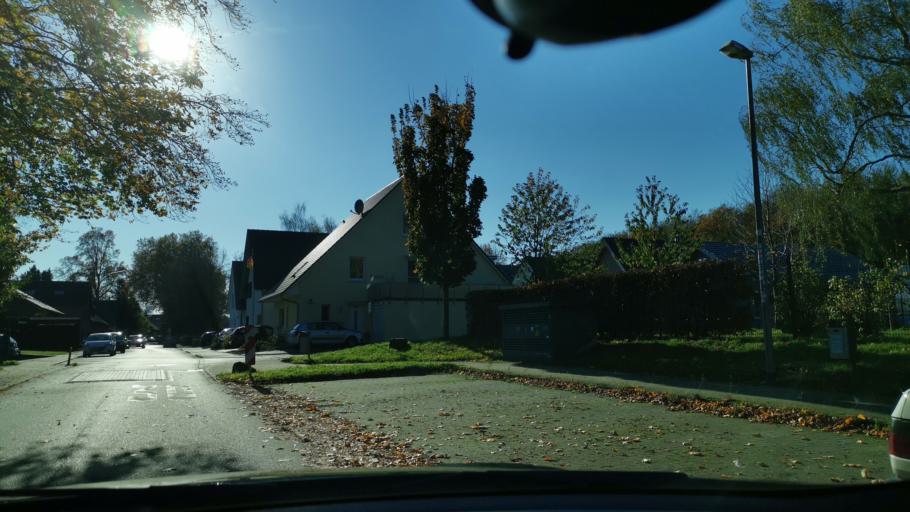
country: DE
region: North Rhine-Westphalia
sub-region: Regierungsbezirk Dusseldorf
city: Rommerskirchen
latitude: 51.0554
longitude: 6.7095
